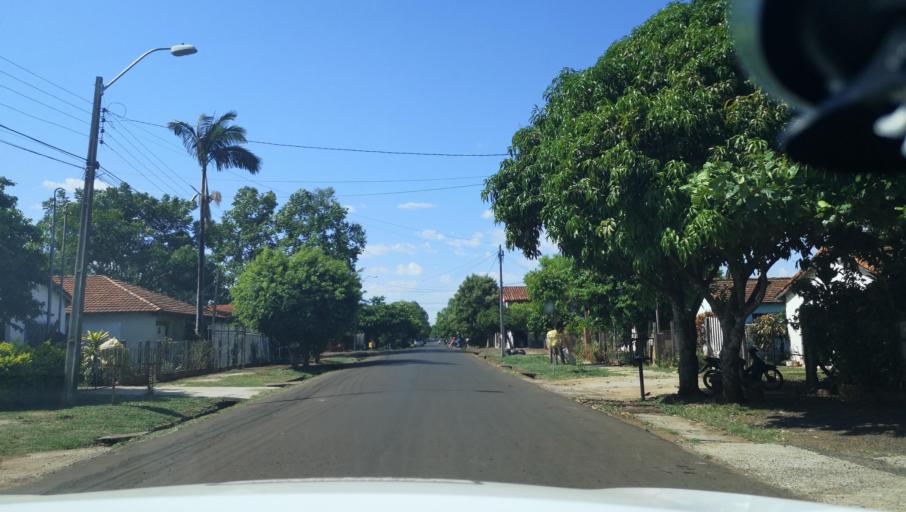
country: PY
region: Itapua
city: Carmen del Parana
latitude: -27.1657
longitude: -56.2337
